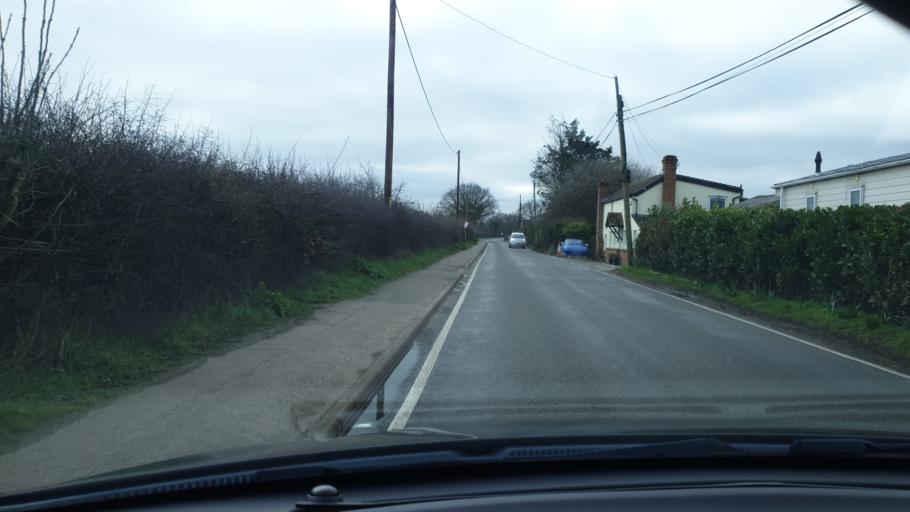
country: GB
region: England
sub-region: Essex
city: Great Bentley
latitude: 51.8472
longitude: 1.0675
